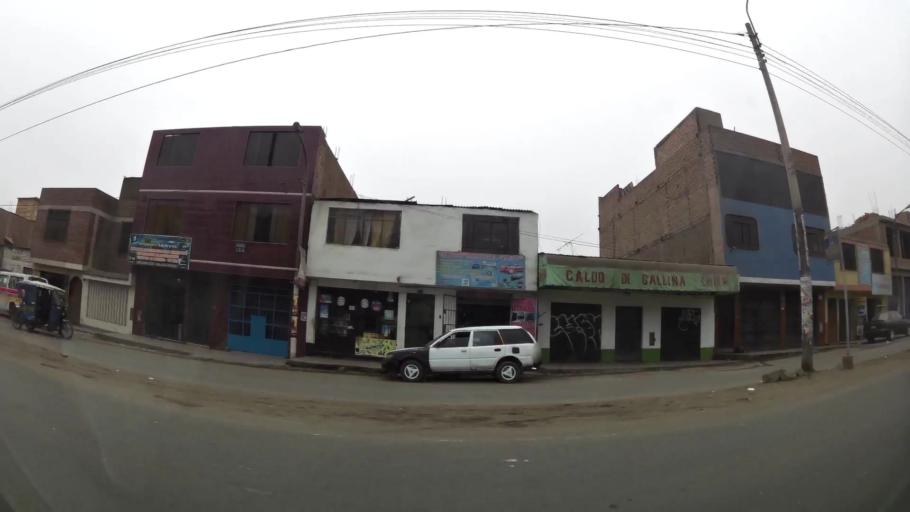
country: PE
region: Lima
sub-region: Lima
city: Urb. Santo Domingo
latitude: -11.8808
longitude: -77.0223
